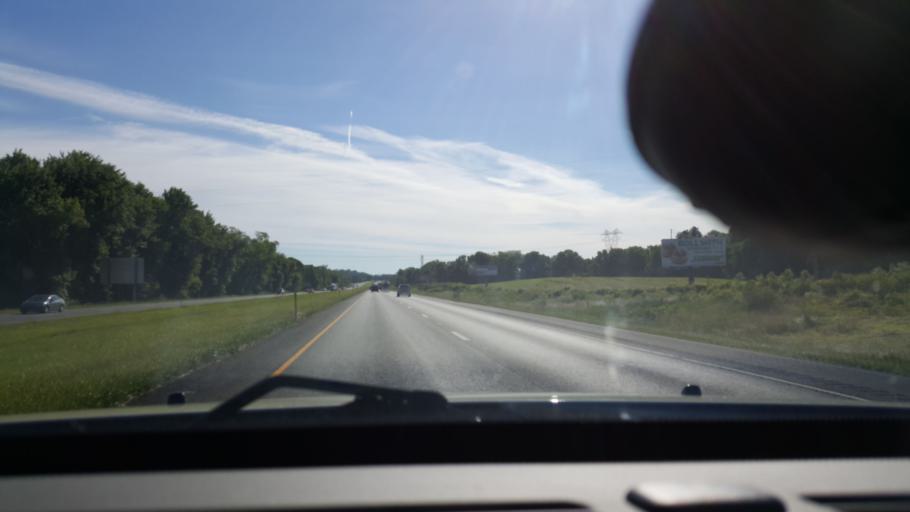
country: US
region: Pennsylvania
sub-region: York County
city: Yorklyn
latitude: 40.0003
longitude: -76.6346
